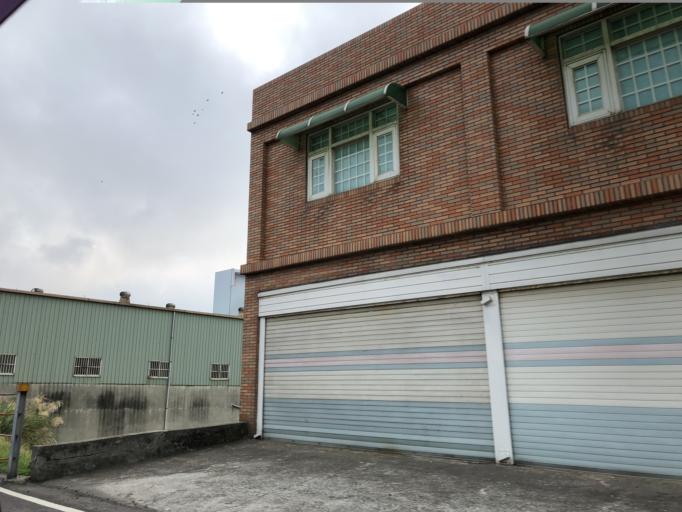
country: TW
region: Taiwan
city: Taoyuan City
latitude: 25.1042
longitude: 121.2470
